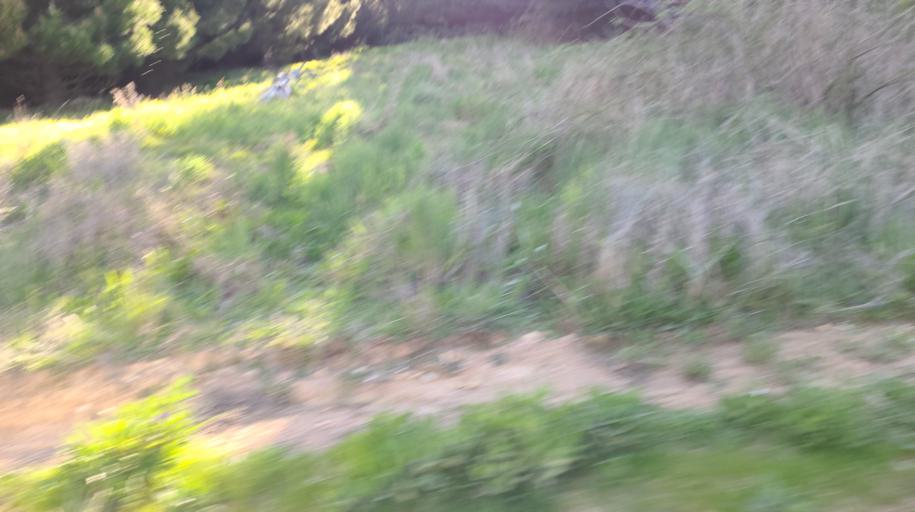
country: AU
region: New South Wales
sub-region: Blayney
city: Millthorpe
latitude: -33.4027
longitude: 149.3119
